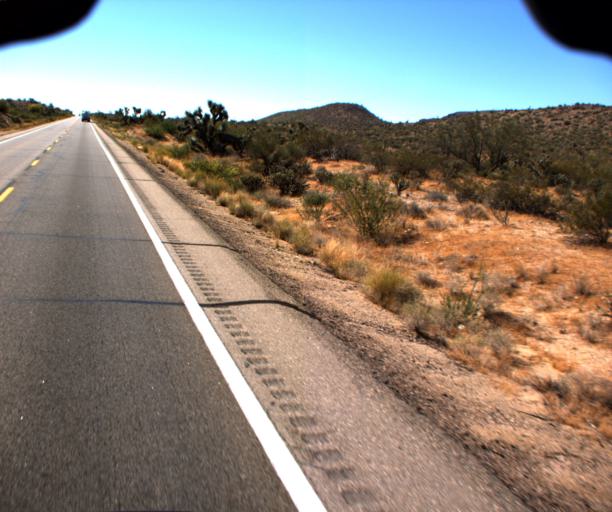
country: US
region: Arizona
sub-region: Yavapai County
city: Bagdad
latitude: 34.3538
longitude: -113.1668
